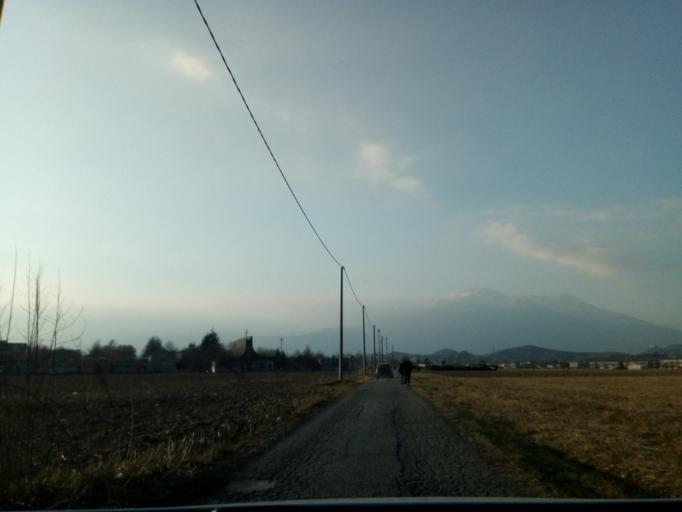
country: IT
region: Piedmont
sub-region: Provincia di Torino
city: Cascinette d'Ivrea
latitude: 45.4625
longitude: 7.9131
